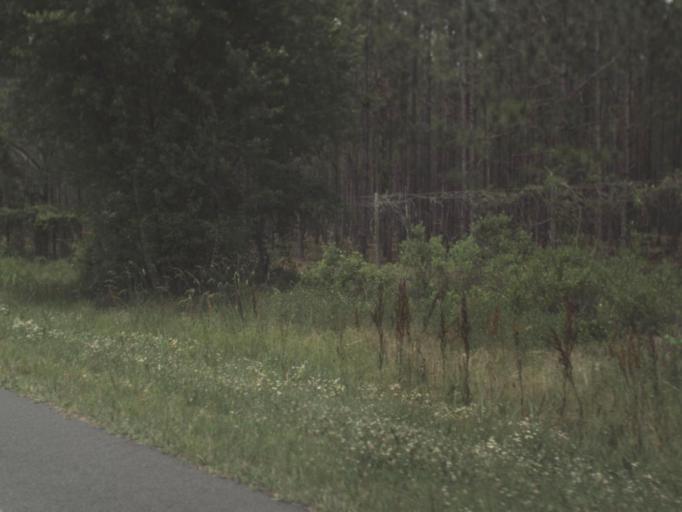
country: US
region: Florida
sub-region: Hamilton County
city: Jasper
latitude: 30.5128
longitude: -82.6697
